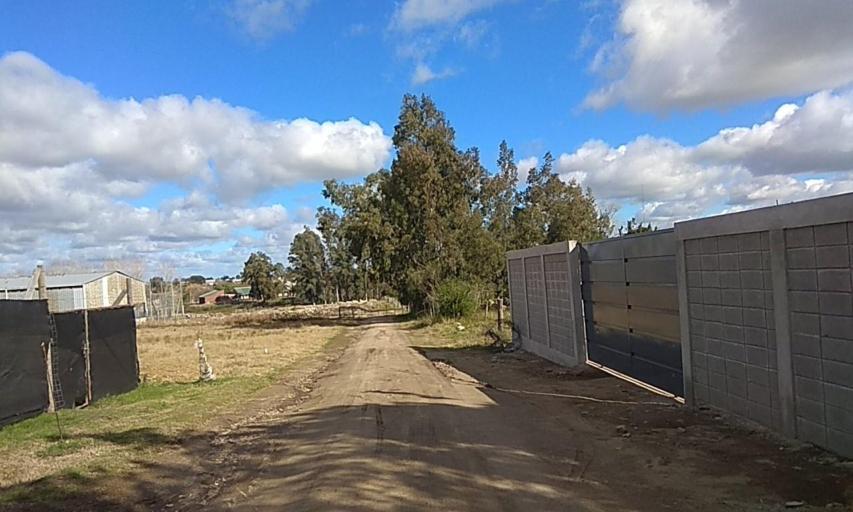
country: UY
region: Florida
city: Florida
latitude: -34.0883
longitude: -56.2236
